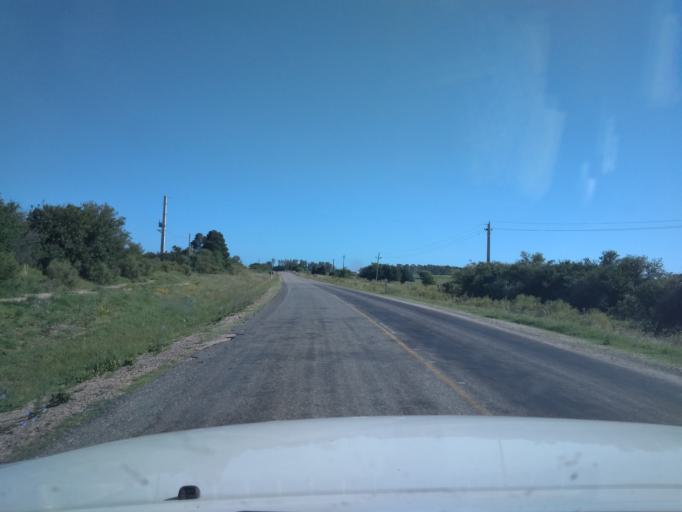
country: UY
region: Canelones
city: San Ramon
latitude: -34.2638
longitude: -55.9278
